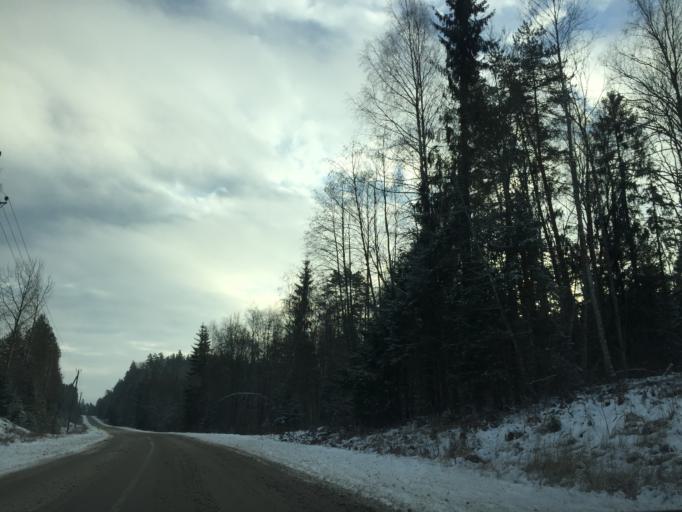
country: LV
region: Amatas Novads
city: Drabesi
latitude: 57.2195
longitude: 25.2886
